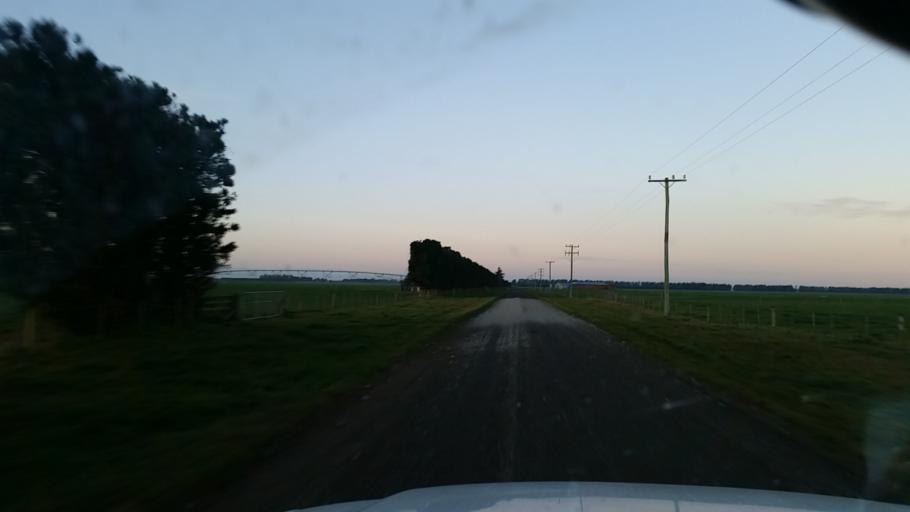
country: NZ
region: Canterbury
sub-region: Ashburton District
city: Tinwald
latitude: -43.9493
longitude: 171.5890
